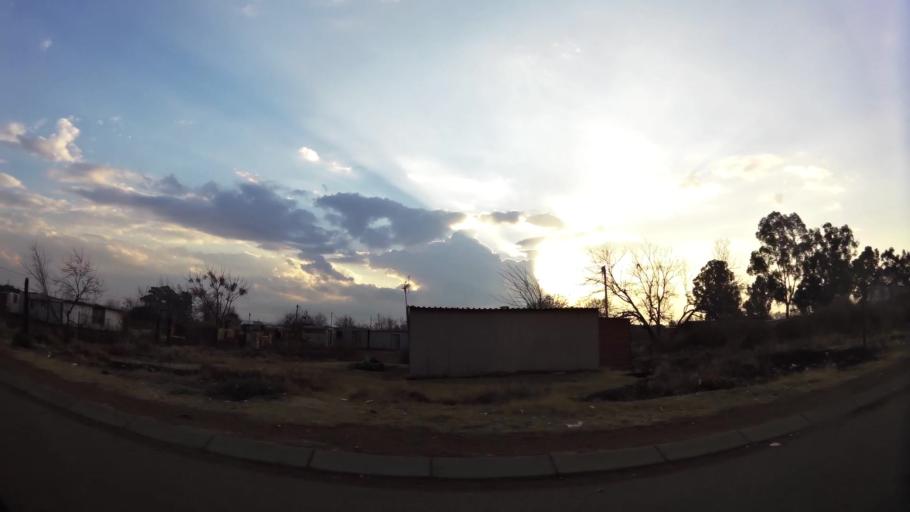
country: ZA
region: Gauteng
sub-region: City of Johannesburg Metropolitan Municipality
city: Orange Farm
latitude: -26.5383
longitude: 27.8499
